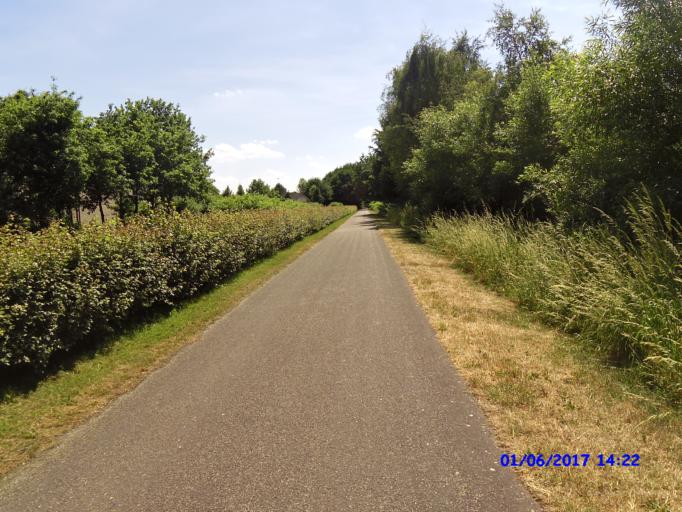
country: NL
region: North Brabant
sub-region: Gemeente Baarle-Nassau
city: Baarle-Nassau
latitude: 51.4325
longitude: 4.9287
